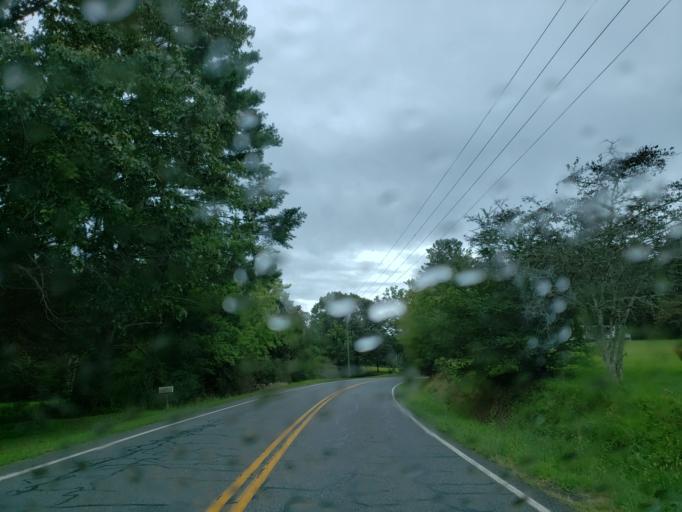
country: US
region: Georgia
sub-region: Gilmer County
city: Ellijay
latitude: 34.6244
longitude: -84.5781
